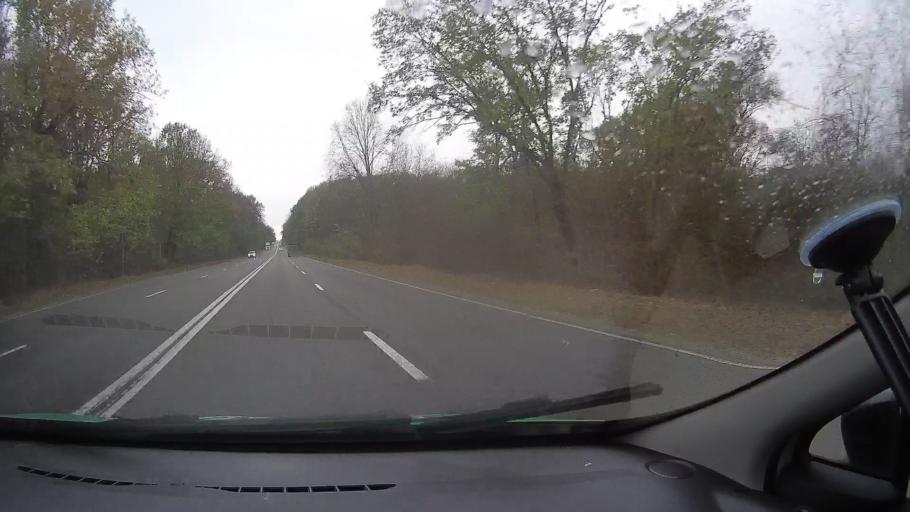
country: RO
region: Constanta
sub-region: Comuna Valu lui Traian
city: Valu lui Traian
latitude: 44.1653
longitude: 28.5049
